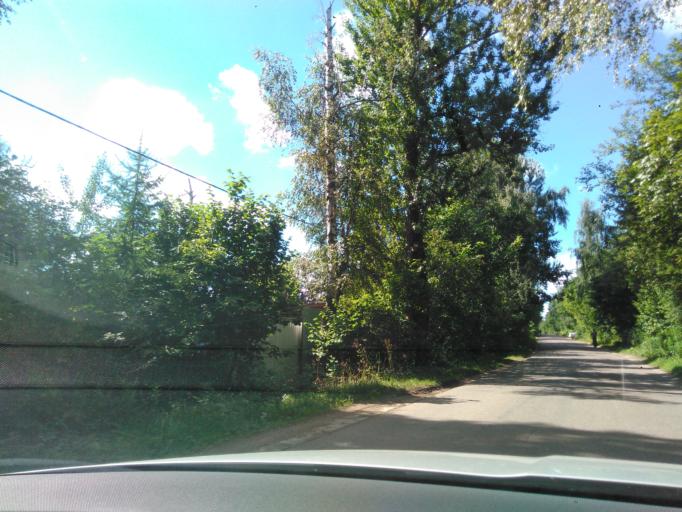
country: RU
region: Moskovskaya
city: Klin
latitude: 56.2302
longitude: 36.8156
